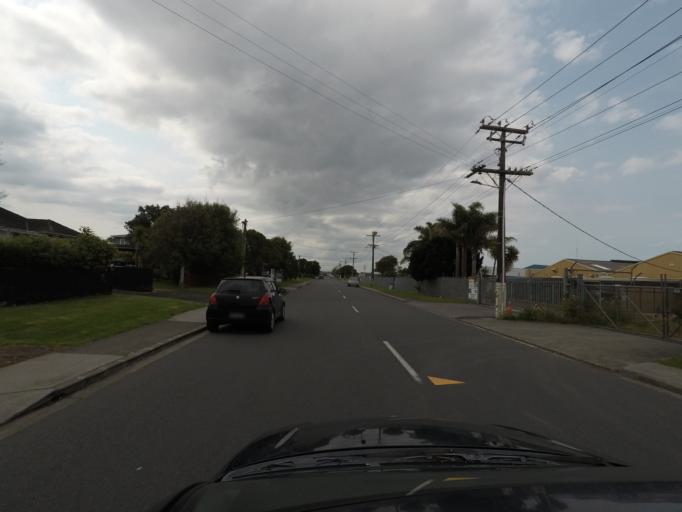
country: NZ
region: Auckland
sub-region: Auckland
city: Rosebank
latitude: -36.8306
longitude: 174.6467
